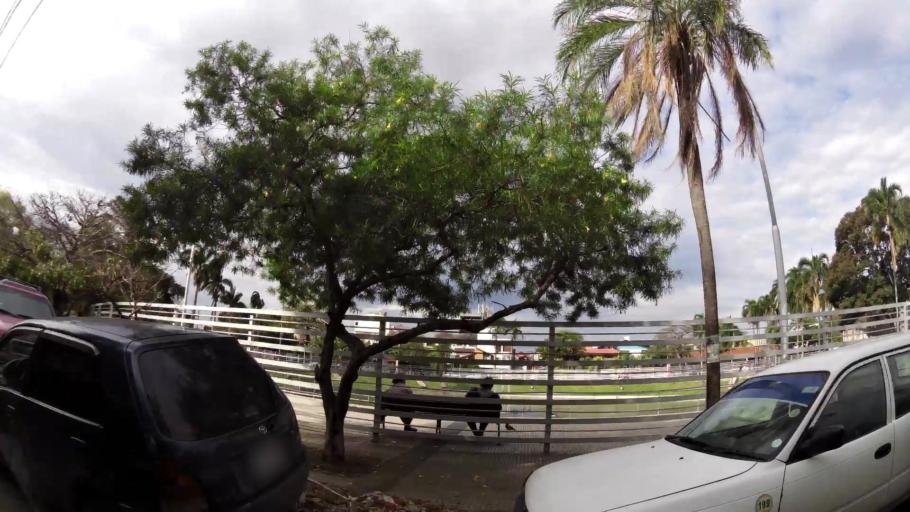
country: BO
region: Santa Cruz
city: Santa Cruz de la Sierra
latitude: -17.7772
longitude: -63.1809
